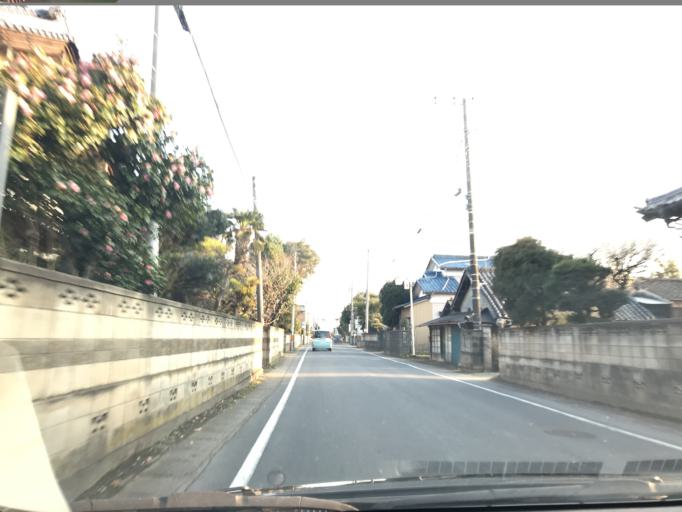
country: JP
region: Ibaraki
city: Ushiku
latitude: 36.0279
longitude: 140.0734
